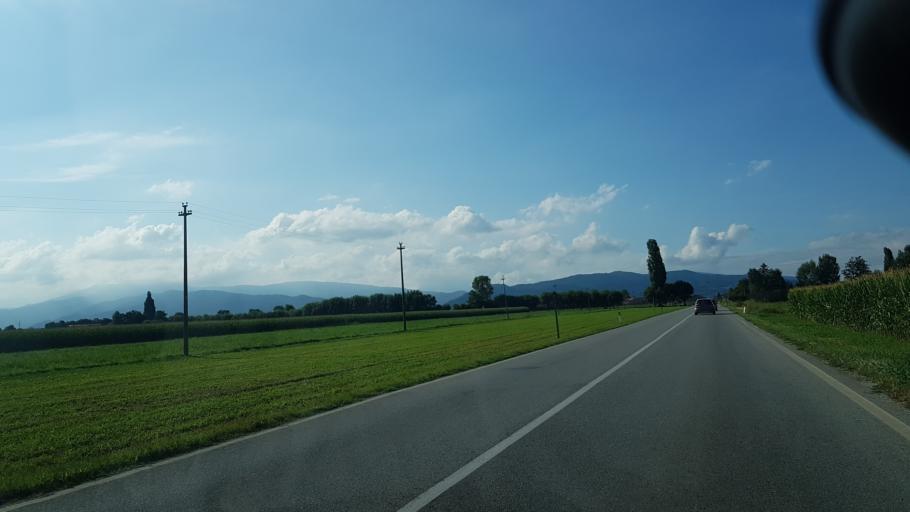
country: IT
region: Piedmont
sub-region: Provincia di Cuneo
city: Roata Rossi
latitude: 44.4650
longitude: 7.5157
